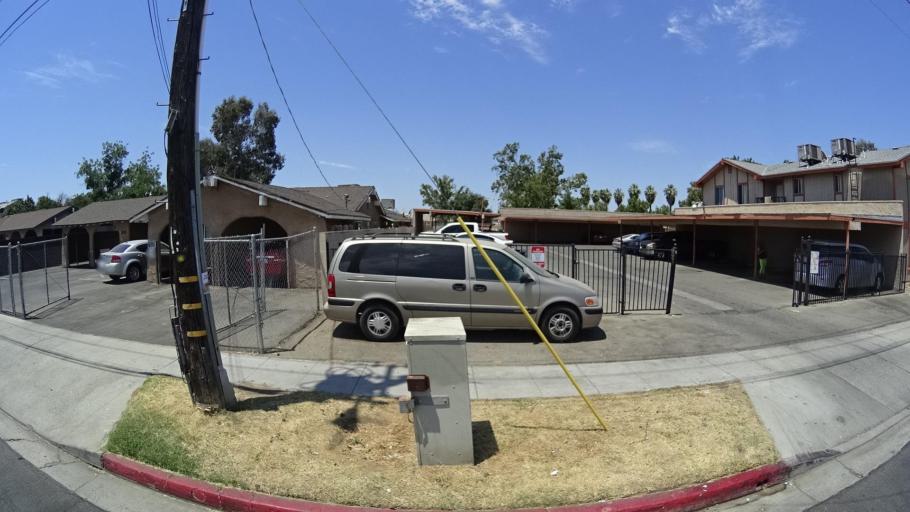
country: US
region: California
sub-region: Fresno County
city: Fresno
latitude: 36.7280
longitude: -119.7512
